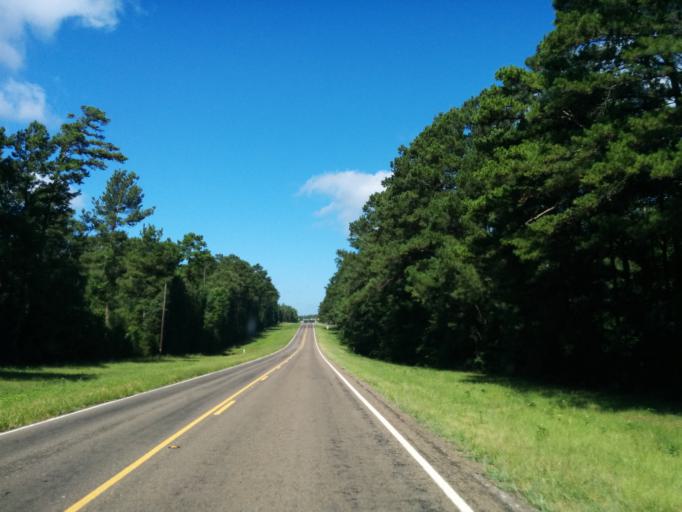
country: US
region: Texas
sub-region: San Augustine County
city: San Augustine
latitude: 31.4098
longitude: -94.0291
